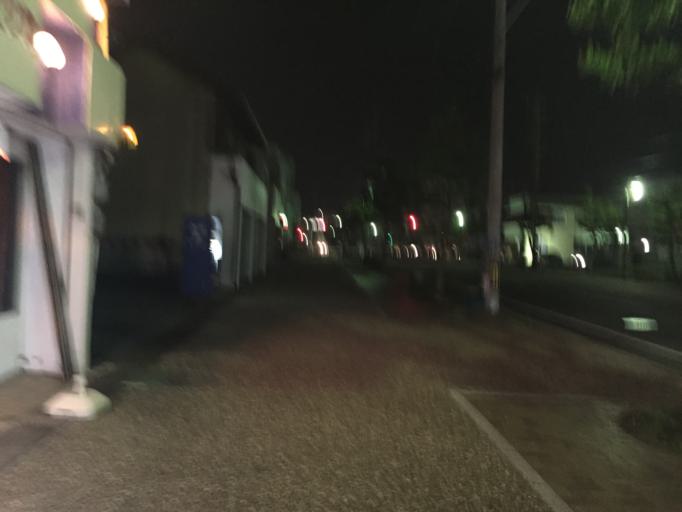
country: JP
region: Mie
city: Yokkaichi
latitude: 34.9671
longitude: 136.6318
